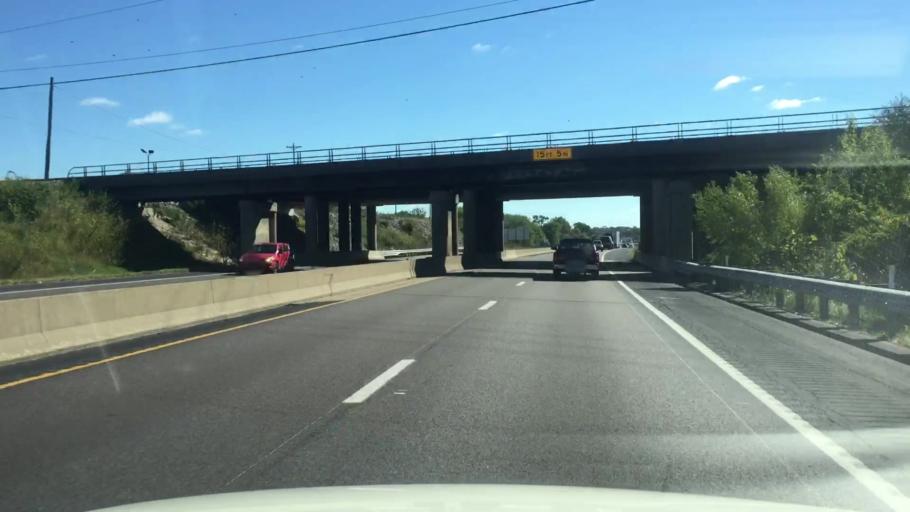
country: US
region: Missouri
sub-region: Boone County
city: Columbia
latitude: 38.9673
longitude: -92.3089
